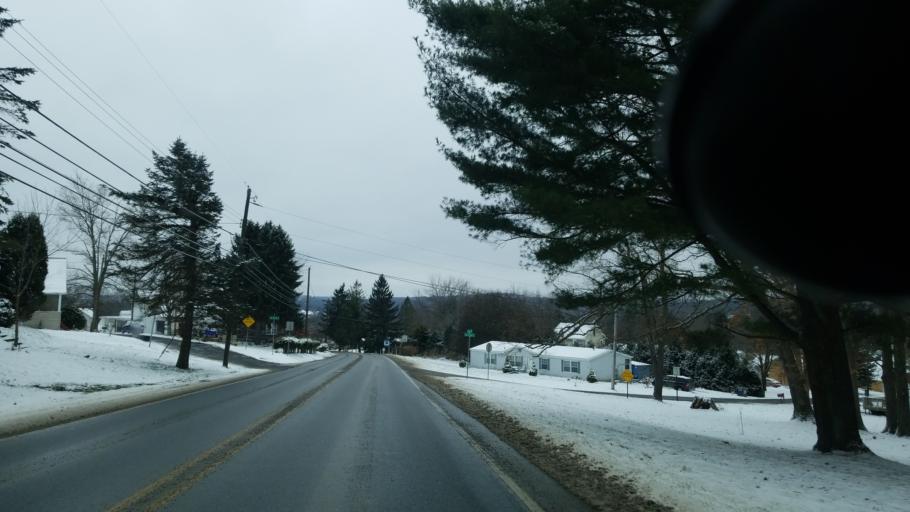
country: US
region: Pennsylvania
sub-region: Jefferson County
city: Albion
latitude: 40.9410
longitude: -78.9498
